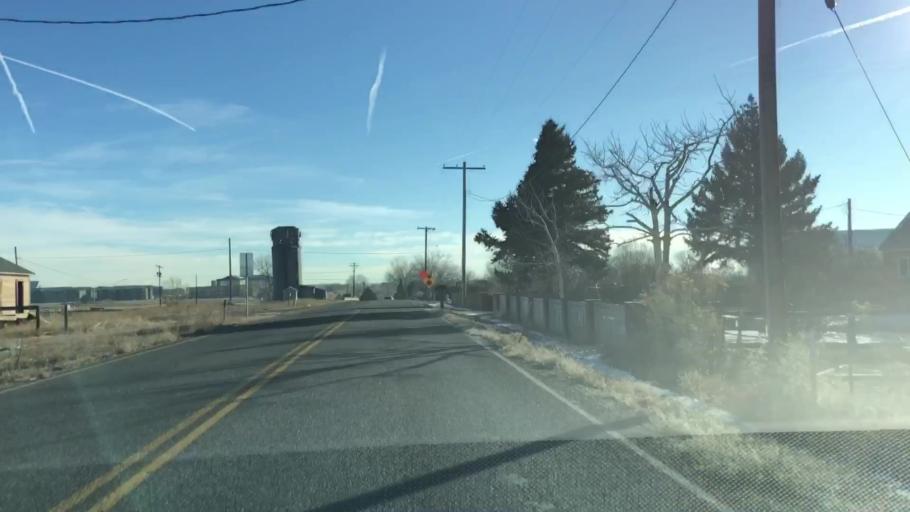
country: US
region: Colorado
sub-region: Larimer County
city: Loveland
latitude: 40.3996
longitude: -104.9953
